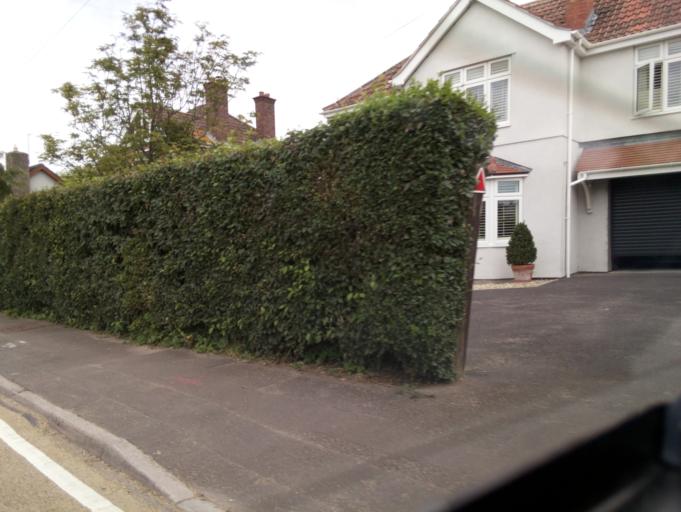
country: GB
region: England
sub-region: Somerset
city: Cheddar
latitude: 51.2810
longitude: -2.7891
